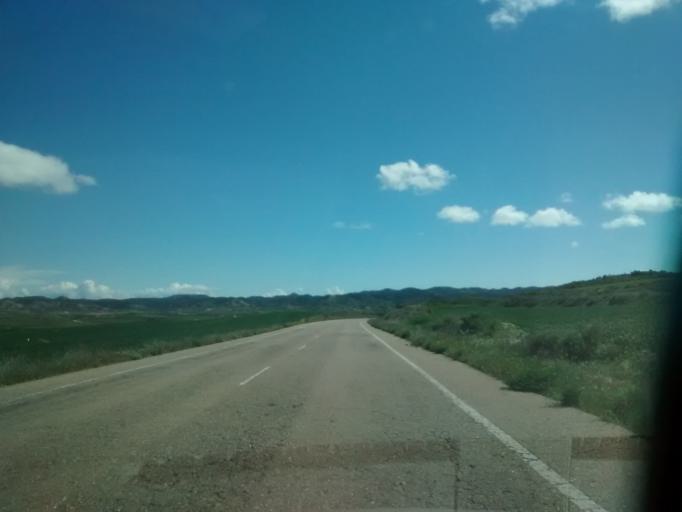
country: ES
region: Aragon
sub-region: Provincia de Zaragoza
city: Lecinena
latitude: 41.8060
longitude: -0.5951
